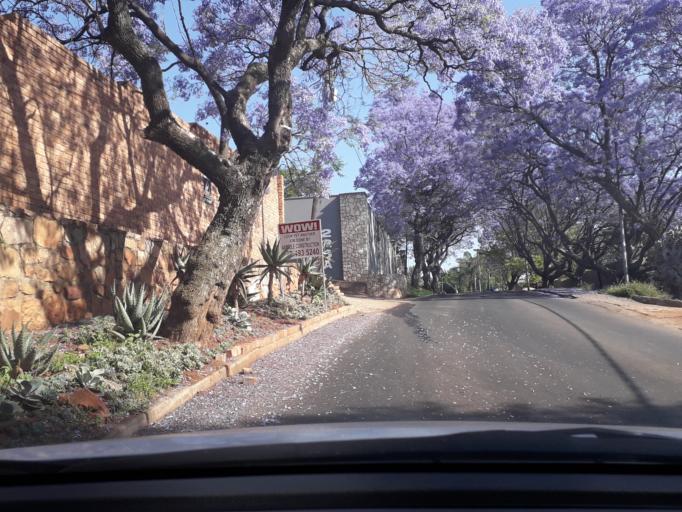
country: ZA
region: Gauteng
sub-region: City of Johannesburg Metropolitan Municipality
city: Johannesburg
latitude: -26.1444
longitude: 27.9761
